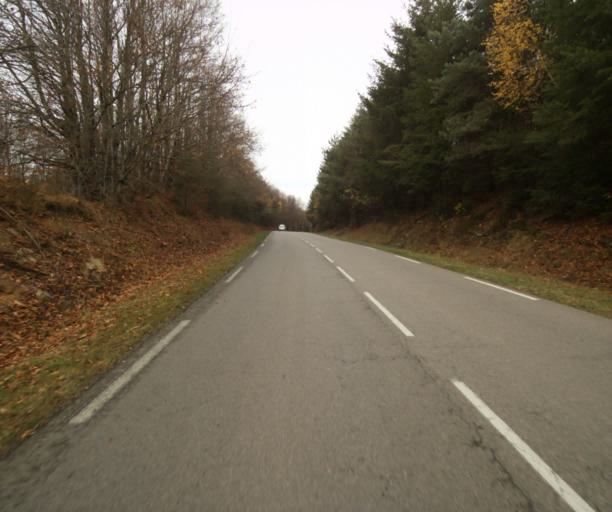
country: FR
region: Limousin
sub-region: Departement de la Correze
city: Sainte-Fortunade
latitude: 45.1810
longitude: 1.7609
